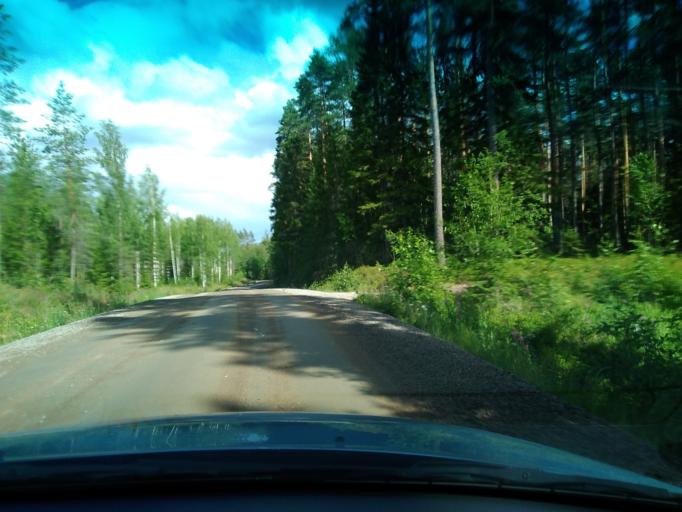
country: FI
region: Central Finland
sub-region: Saarijaervi-Viitasaari
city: Saarijaervi
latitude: 62.7323
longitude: 25.1149
